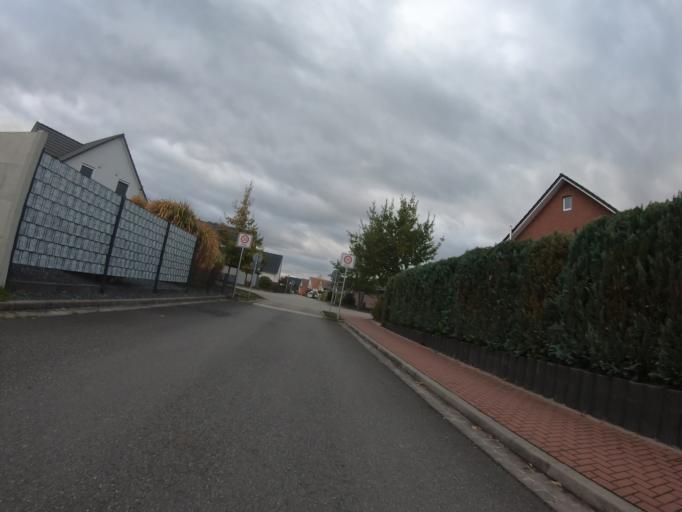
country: DE
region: Lower Saxony
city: Isenbuttel
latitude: 52.4426
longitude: 10.5766
